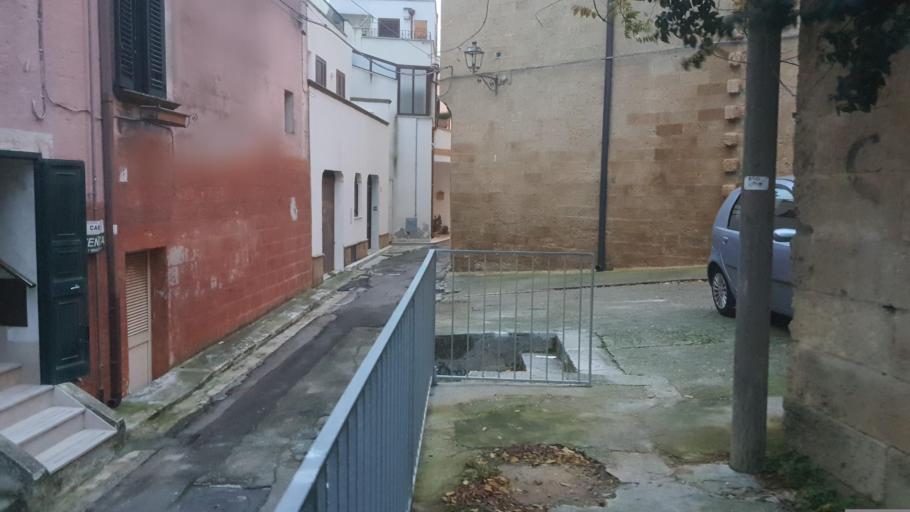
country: IT
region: Apulia
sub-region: Provincia di Lecce
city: Tricase
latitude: 39.9319
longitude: 18.3618
